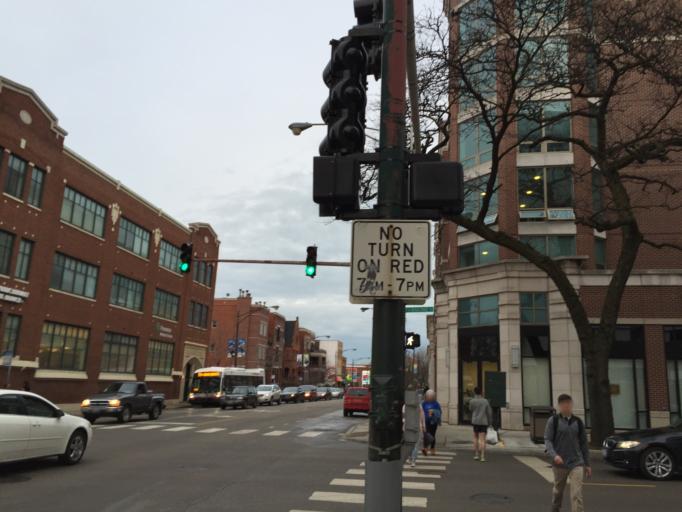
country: US
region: Illinois
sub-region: Cook County
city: Chicago
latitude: 41.9252
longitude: -87.6586
